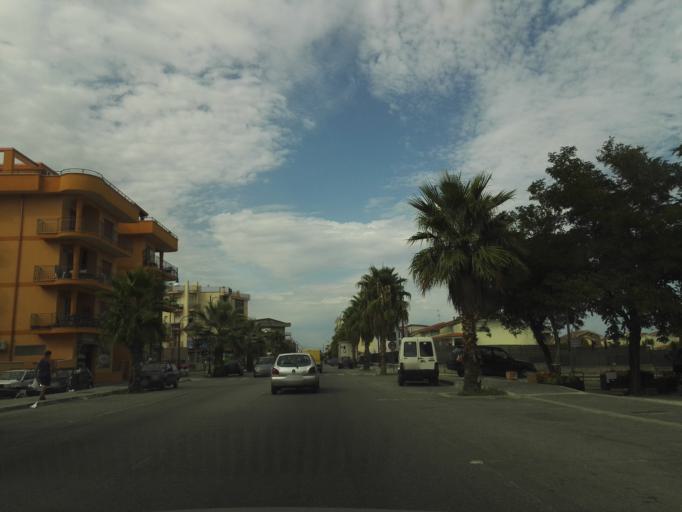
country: IT
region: Calabria
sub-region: Provincia di Catanzaro
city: Marina di Davoli
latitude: 38.6658
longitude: 16.5456
